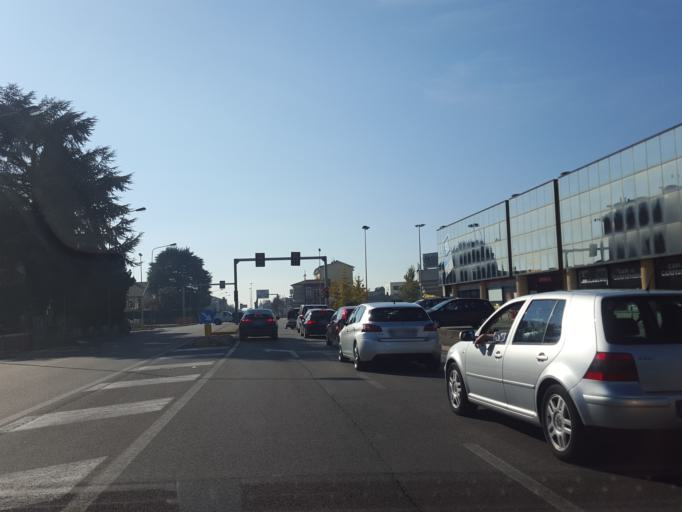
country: IT
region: Veneto
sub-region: Provincia di Vicenza
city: Brendola
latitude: 45.4971
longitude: 11.4331
